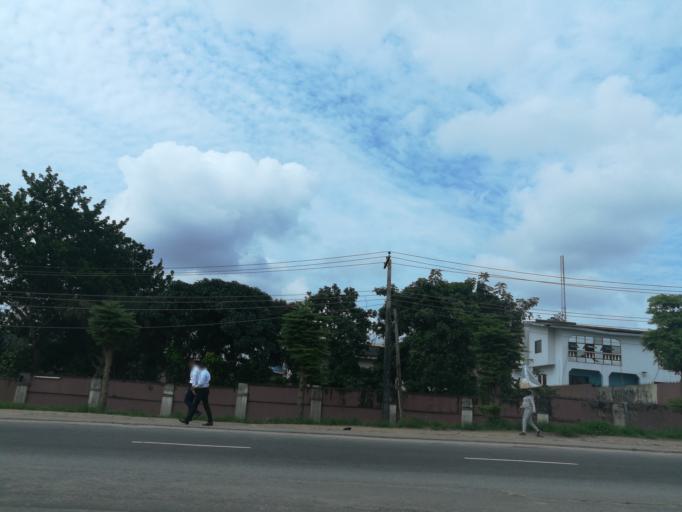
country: NG
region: Lagos
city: Somolu
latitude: 6.5560
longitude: 3.3711
